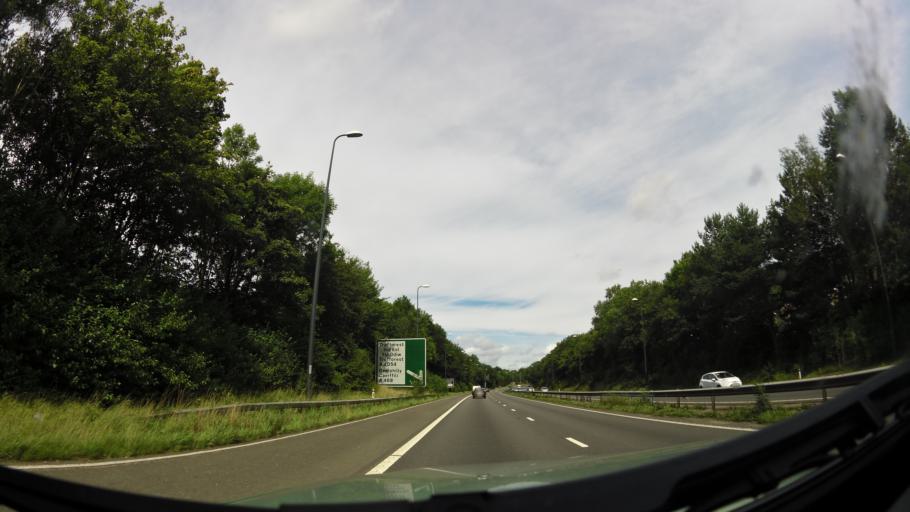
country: GB
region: Wales
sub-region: Cardiff
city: Radyr
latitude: 51.5488
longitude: -3.2680
